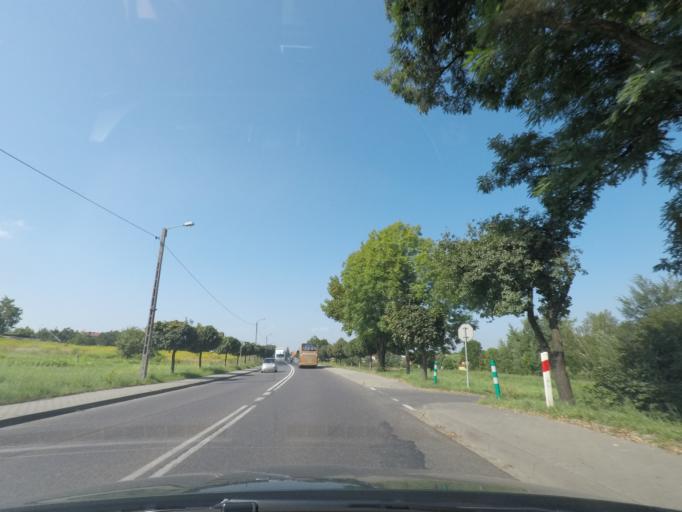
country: PL
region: Lesser Poland Voivodeship
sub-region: Powiat chrzanowski
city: Libiaz
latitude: 50.1053
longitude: 19.3196
